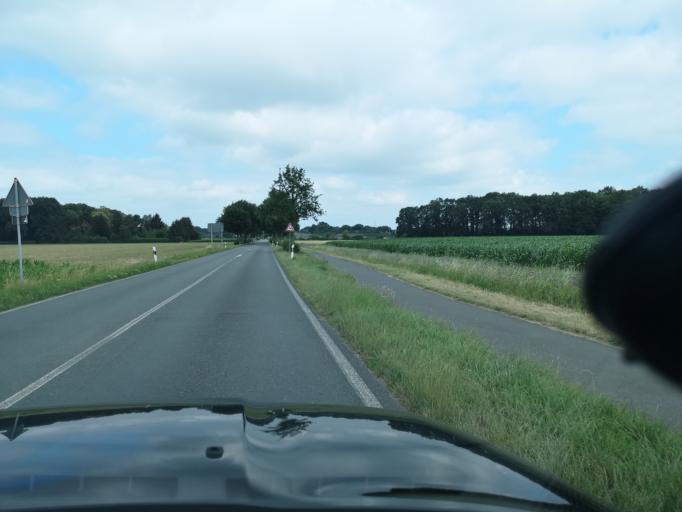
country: DE
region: North Rhine-Westphalia
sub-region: Regierungsbezirk Dusseldorf
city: Wesel
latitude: 51.6757
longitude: 6.6429
